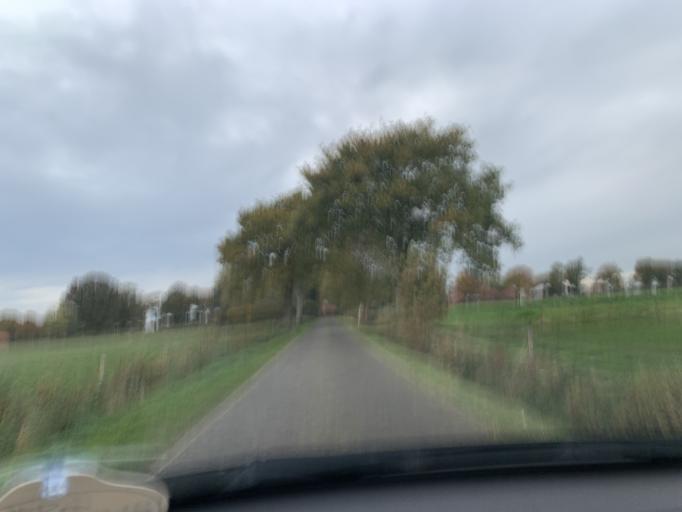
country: DE
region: Lower Saxony
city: Wiefelstede
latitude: 53.2705
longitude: 8.0426
